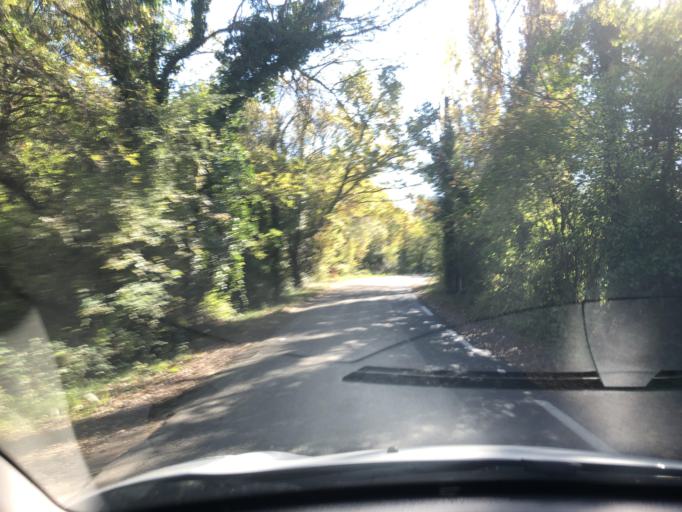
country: FR
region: Provence-Alpes-Cote d'Azur
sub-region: Departement du Vaucluse
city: Althen-des-Paluds
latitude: 43.9811
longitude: 4.9424
